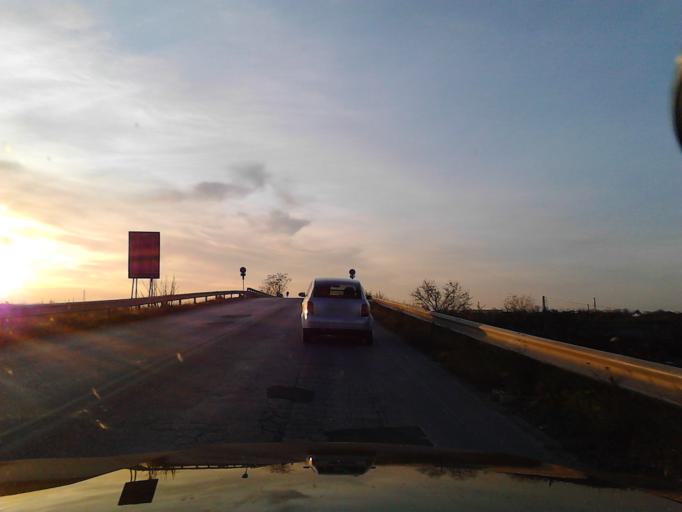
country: IT
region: Apulia
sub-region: Provincia di Bari
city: Triggiano
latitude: 41.0567
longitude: 16.9196
